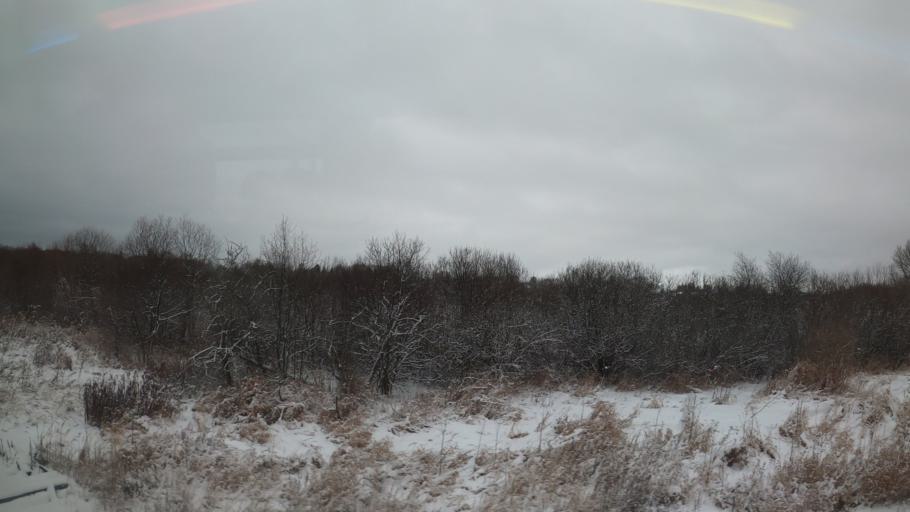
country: RU
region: Jaroslavl
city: Pereslavl'-Zalesskiy
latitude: 56.7058
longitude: 38.9097
